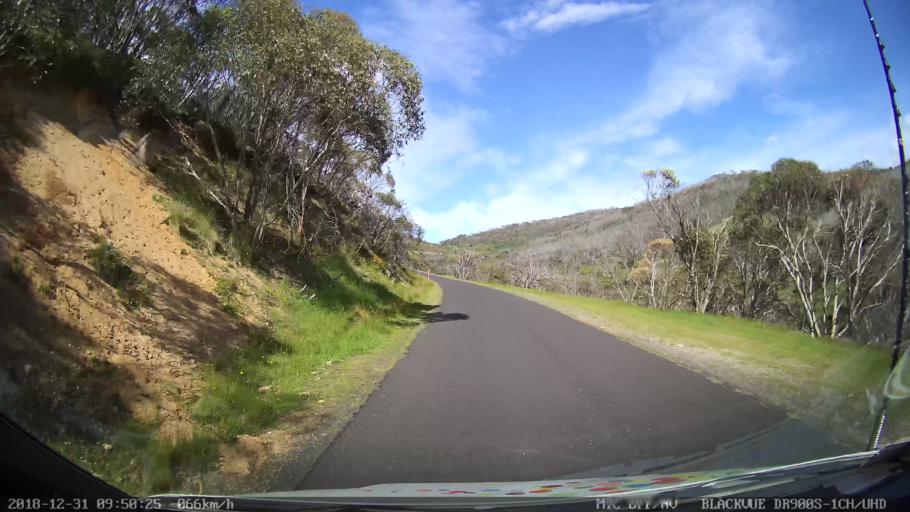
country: AU
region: New South Wales
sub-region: Snowy River
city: Jindabyne
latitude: -36.5202
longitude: 148.2733
